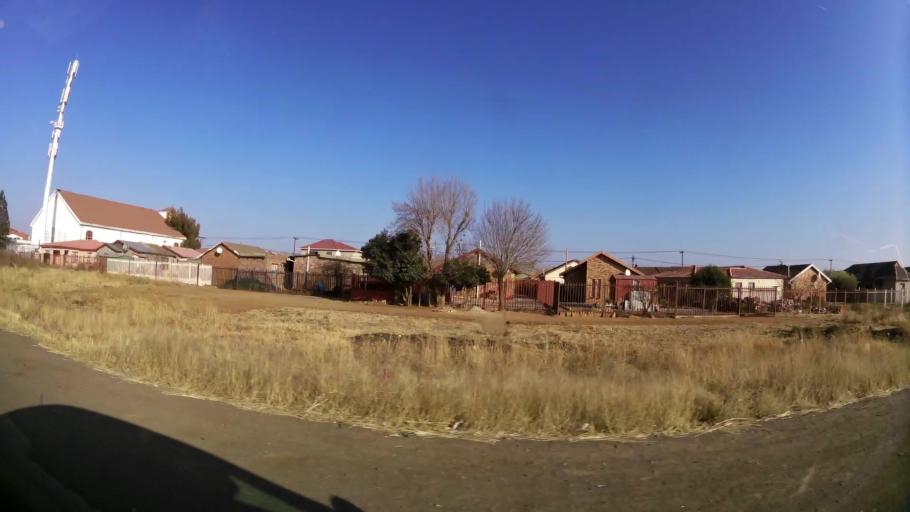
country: ZA
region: Orange Free State
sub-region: Mangaung Metropolitan Municipality
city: Bloemfontein
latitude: -29.1503
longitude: 26.2654
